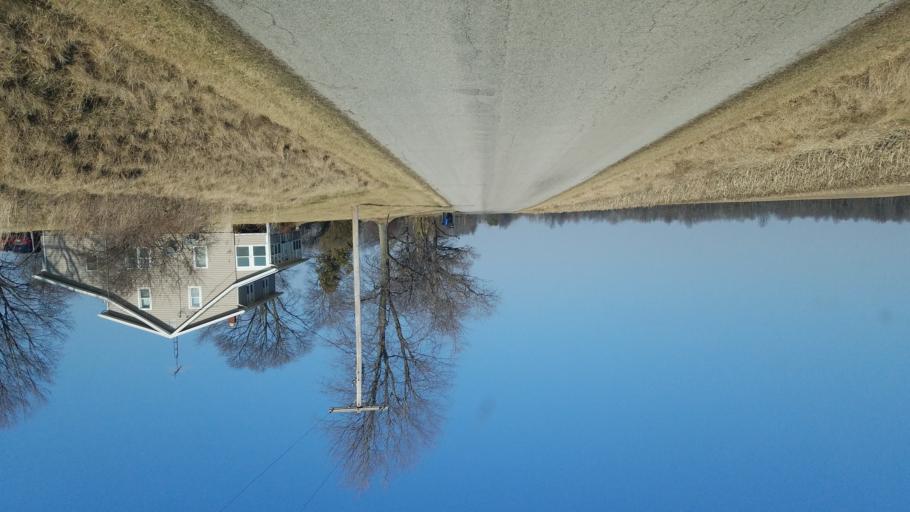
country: US
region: Ohio
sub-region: Crawford County
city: Crestline
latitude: 40.7720
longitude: -82.7651
